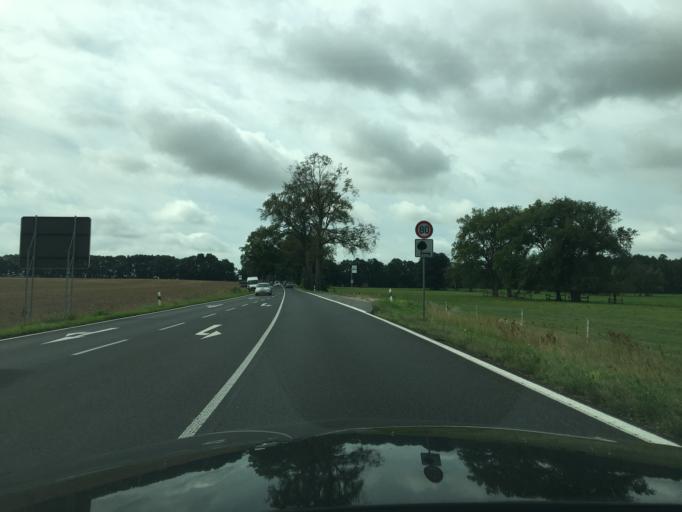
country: DE
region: Brandenburg
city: Gransee
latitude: 52.9658
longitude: 13.1488
